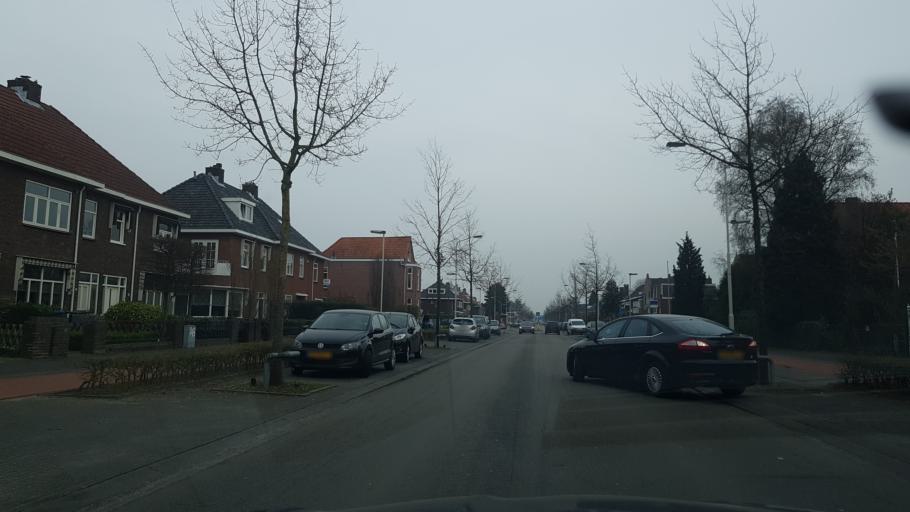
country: NL
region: North Brabant
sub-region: Gemeente Breda
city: Hoge Vucht
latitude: 51.5947
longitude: 4.8128
